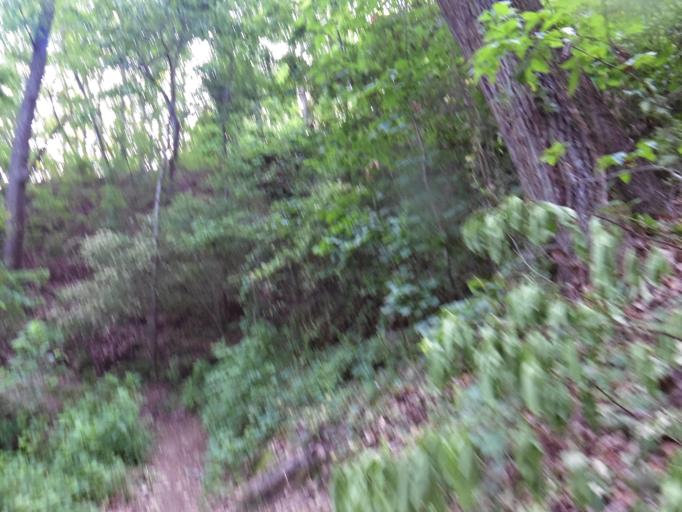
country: US
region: Tennessee
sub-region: Knox County
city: Knoxville
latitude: 36.0033
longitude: -83.9414
